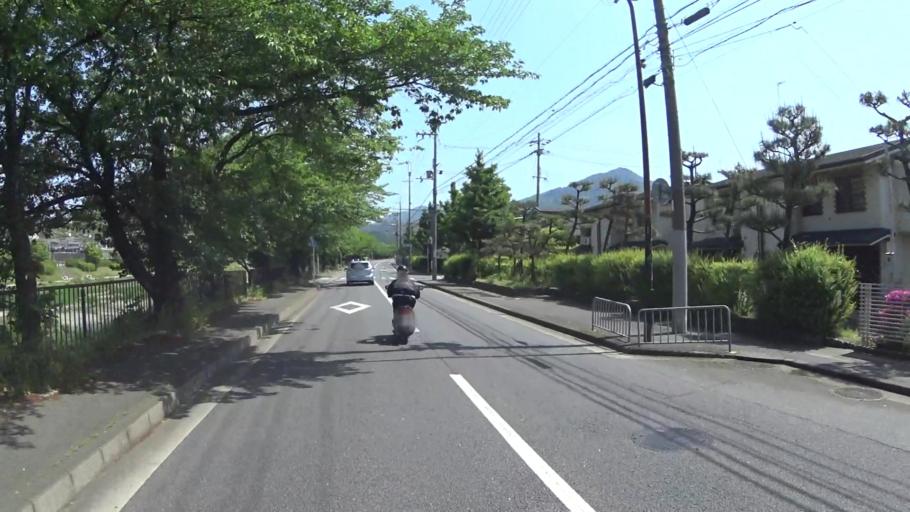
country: JP
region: Kyoto
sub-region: Kyoto-shi
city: Kamigyo-ku
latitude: 35.0444
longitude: 135.7810
